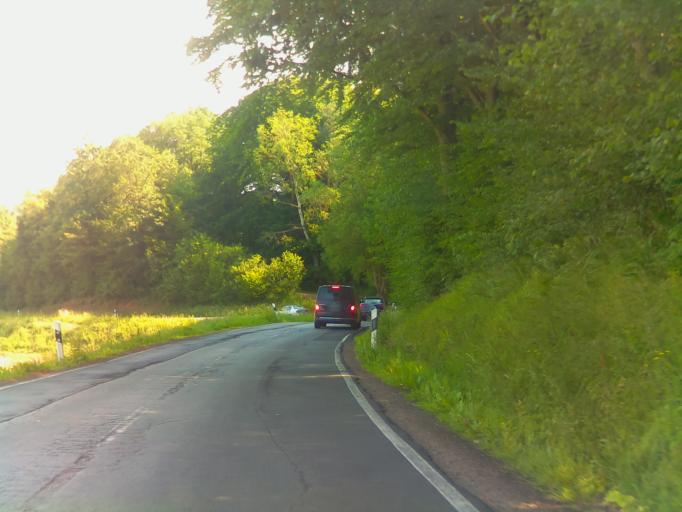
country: DE
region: Hesse
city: Rosenthal
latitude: 50.9630
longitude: 8.8703
